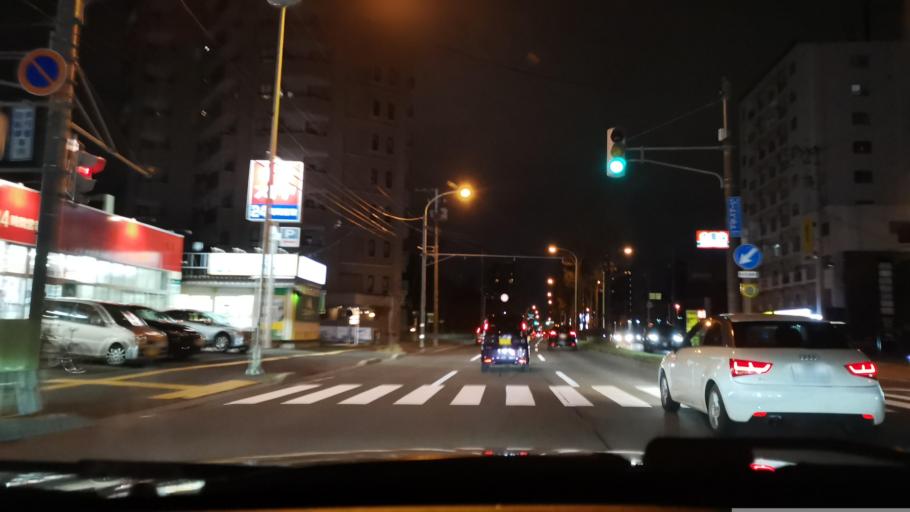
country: JP
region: Hokkaido
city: Sapporo
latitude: 43.0406
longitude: 141.4101
